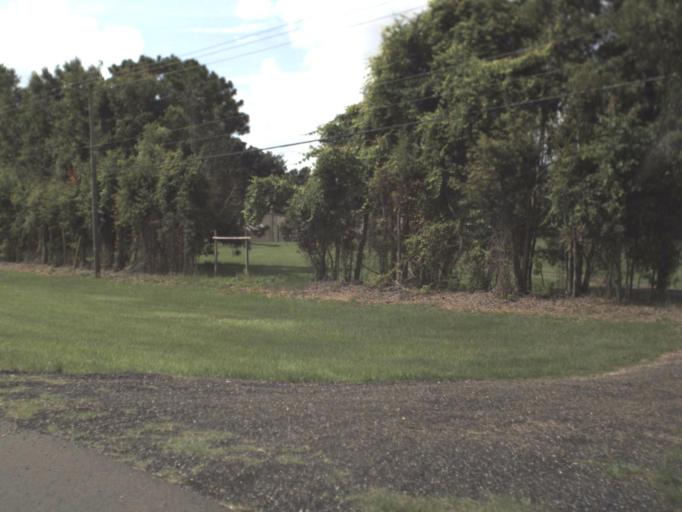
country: US
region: Florida
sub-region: Pasco County
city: Dade City
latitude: 28.3195
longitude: -82.1821
